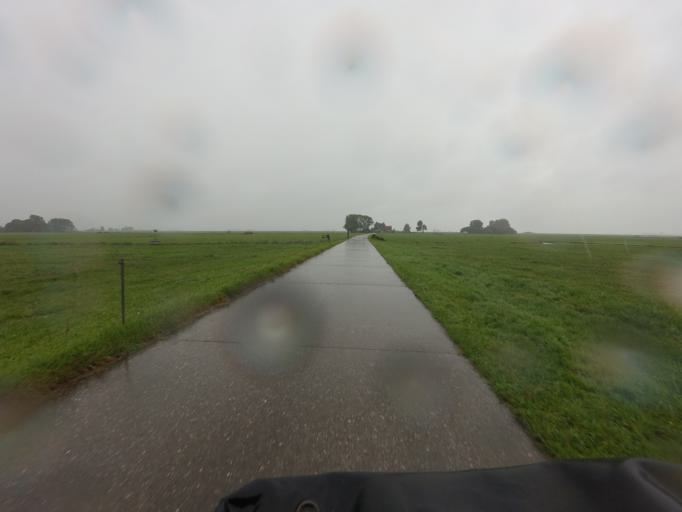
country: NL
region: Friesland
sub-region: Sudwest Fryslan
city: Bolsward
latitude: 53.0063
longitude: 5.5208
